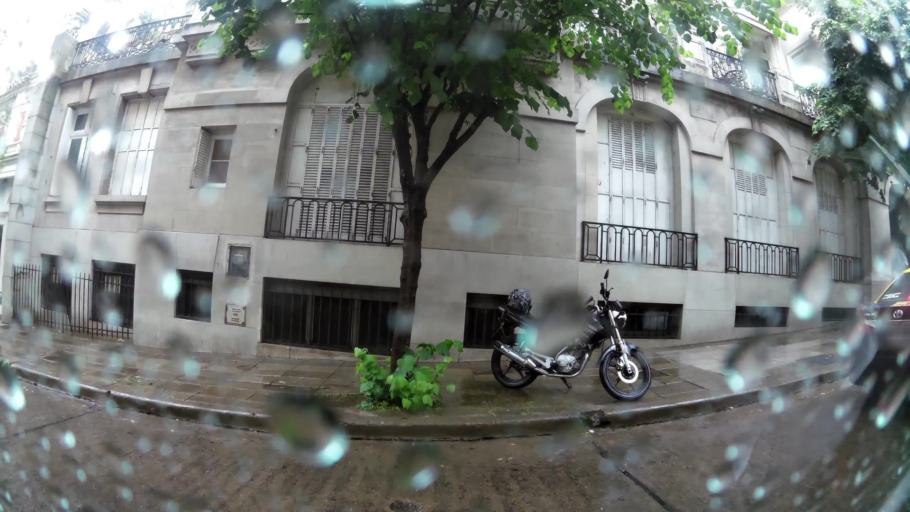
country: AR
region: Buenos Aires F.D.
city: Retiro
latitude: -34.5912
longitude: -58.3831
